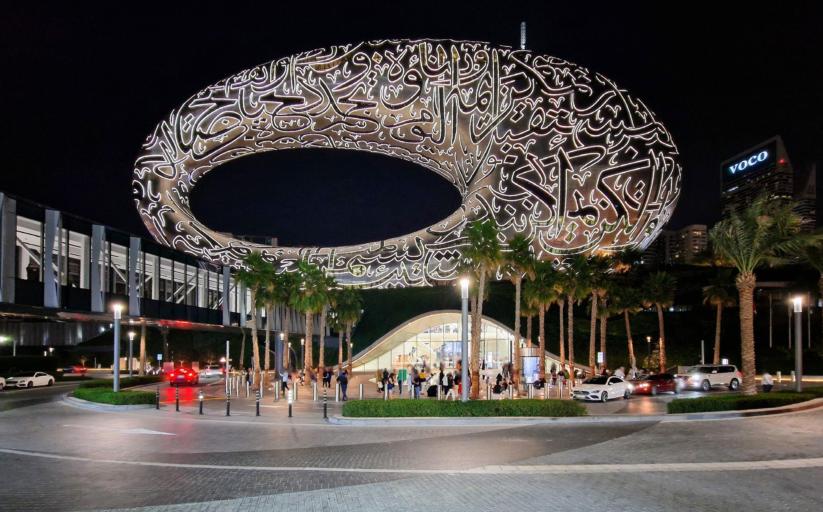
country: AE
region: Ash Shariqah
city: Sharjah
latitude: 25.2186
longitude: 55.2824
